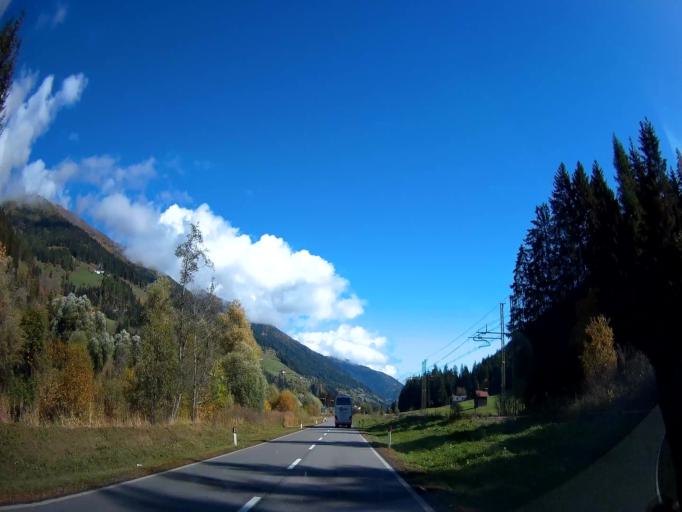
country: IT
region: Trentino-Alto Adige
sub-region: Bolzano
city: Sesto
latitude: 46.7354
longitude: 12.3492
